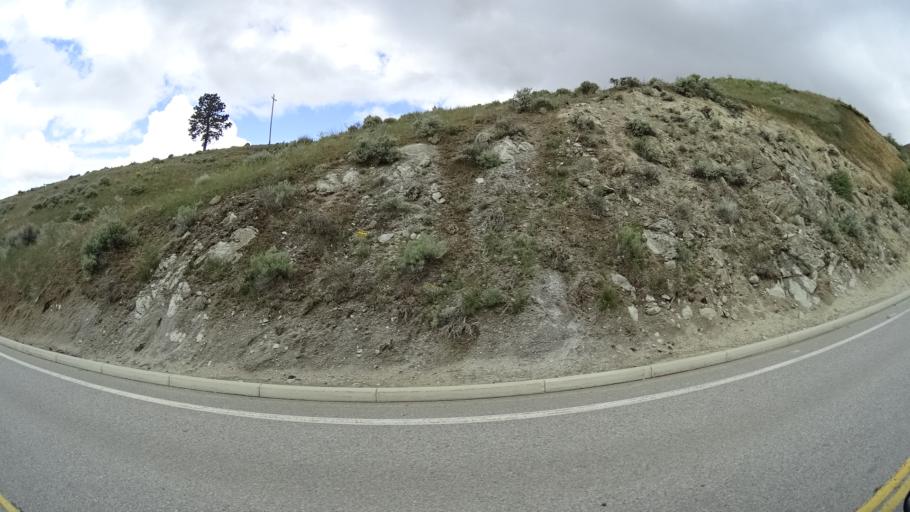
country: US
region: Idaho
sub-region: Ada County
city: Boise
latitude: 43.7159
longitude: -116.1621
